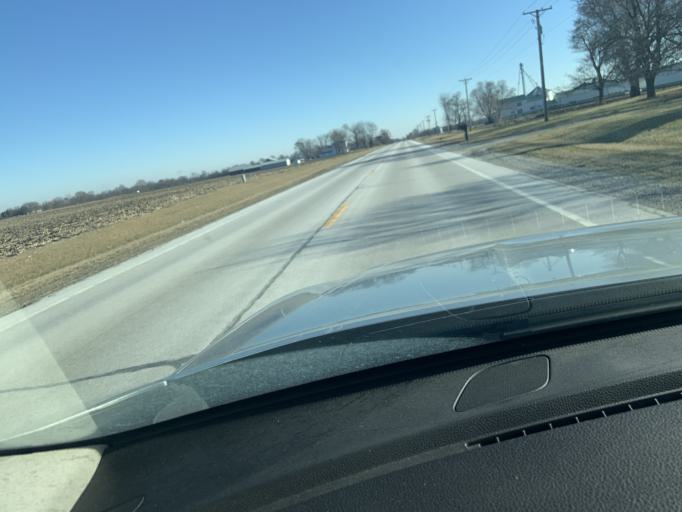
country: US
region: Illinois
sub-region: Grundy County
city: Morris
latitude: 41.3704
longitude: -88.5242
